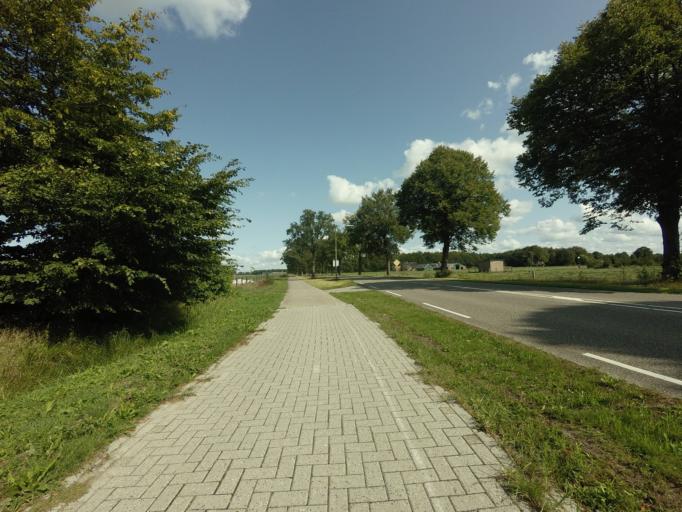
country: NL
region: Overijssel
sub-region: Gemeente Dalfsen
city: Dalfsen
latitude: 52.5291
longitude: 6.2612
